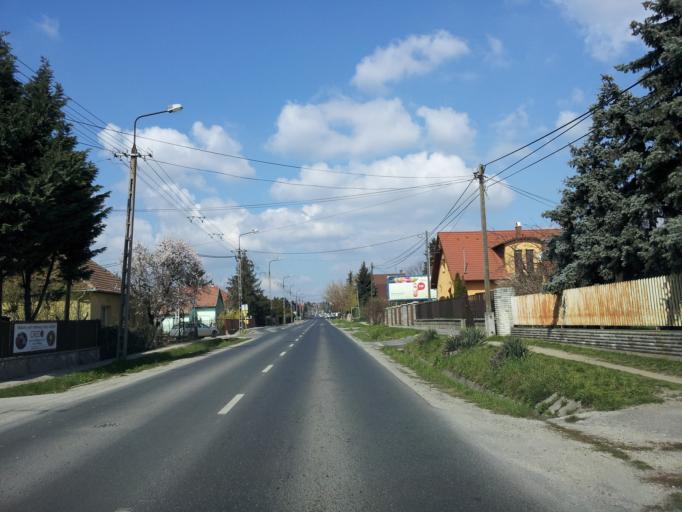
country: HU
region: Pest
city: Erd
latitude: 47.3884
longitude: 18.9220
